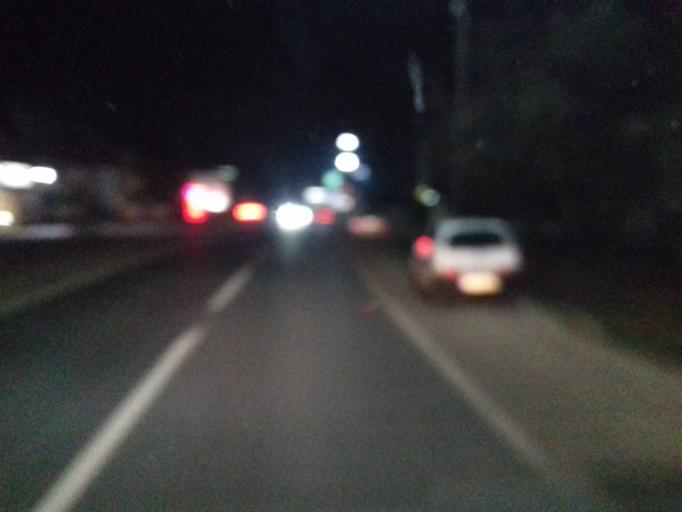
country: BA
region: Federation of Bosnia and Herzegovina
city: Hadzici
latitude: 43.8501
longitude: 18.2388
